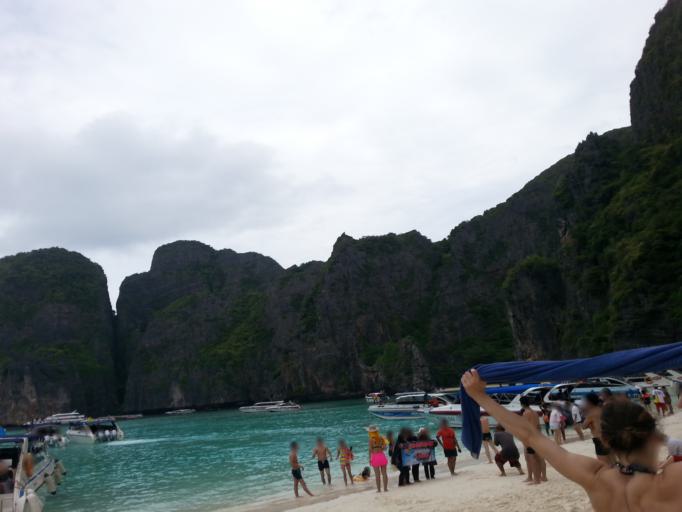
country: TH
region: Krabi
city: Saladan
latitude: 7.6768
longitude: 98.7663
